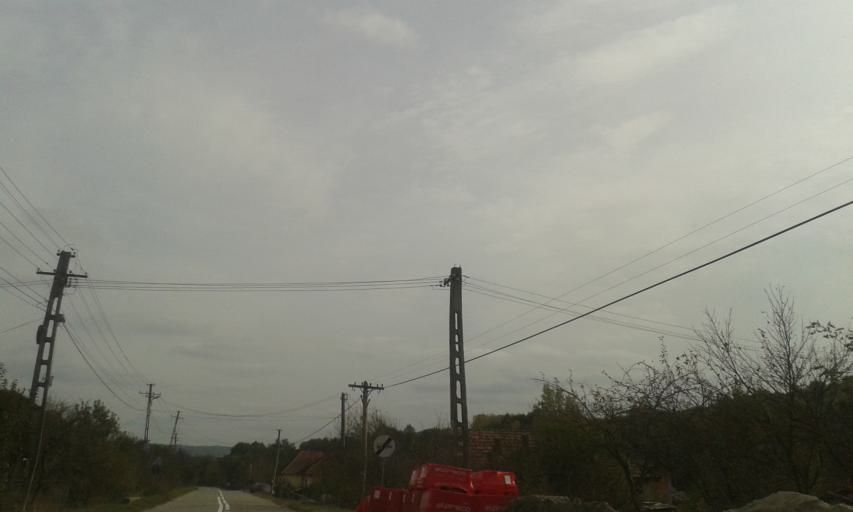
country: RO
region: Valcea
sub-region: Comuna Gradistea
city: Gradistea
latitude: 44.9051
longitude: 23.7959
